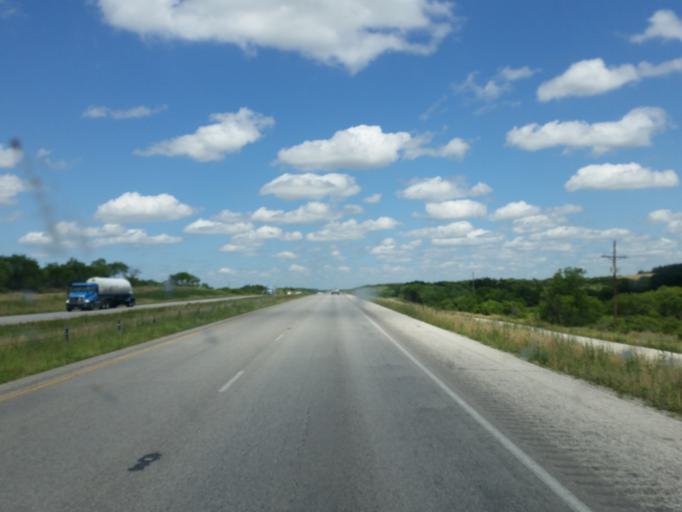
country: US
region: Texas
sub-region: Callahan County
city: Baird
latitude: 32.3829
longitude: -99.2806
